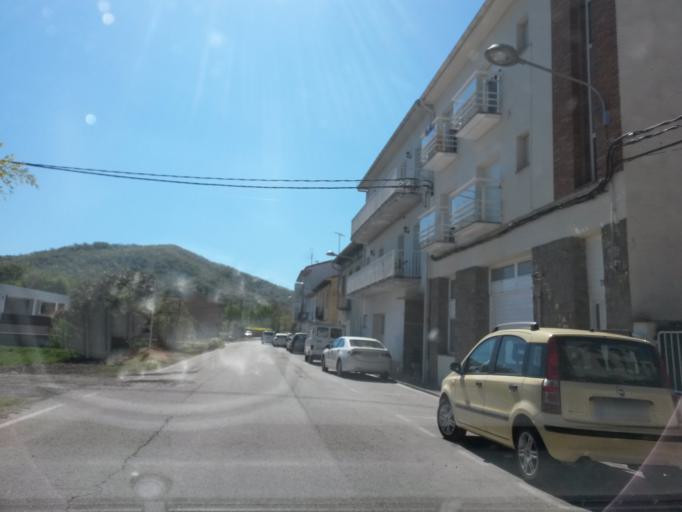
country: ES
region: Catalonia
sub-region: Provincia de Girona
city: Olot
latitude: 42.1688
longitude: 2.4806
